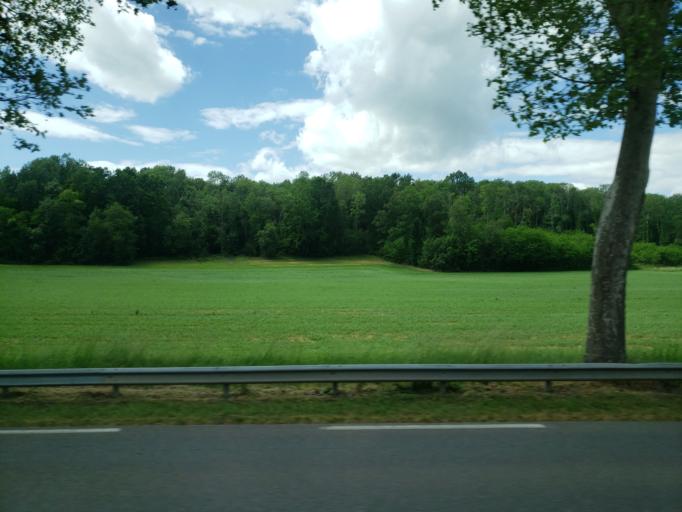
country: FR
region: Bourgogne
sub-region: Departement de l'Yonne
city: Appoigny
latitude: 47.8952
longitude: 3.5208
